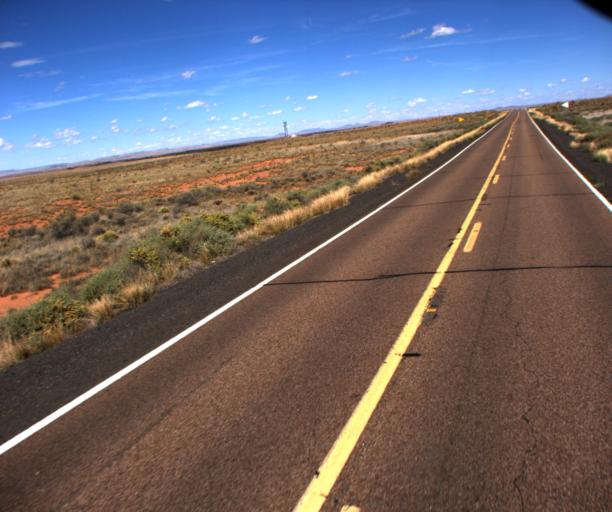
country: US
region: Arizona
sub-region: Navajo County
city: Holbrook
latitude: 34.8269
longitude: -110.1909
